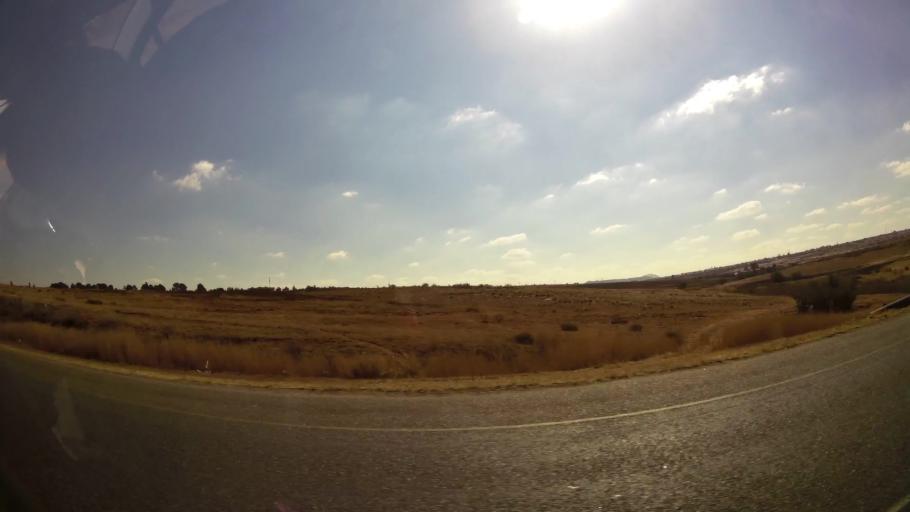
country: ZA
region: Gauteng
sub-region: West Rand District Municipality
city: Randfontein
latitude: -26.1777
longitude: 27.7660
